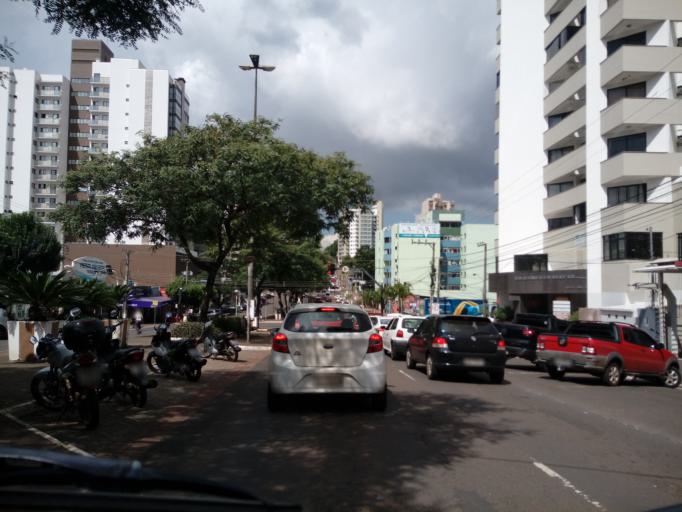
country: BR
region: Santa Catarina
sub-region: Chapeco
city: Chapeco
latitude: -27.1059
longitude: -52.6140
